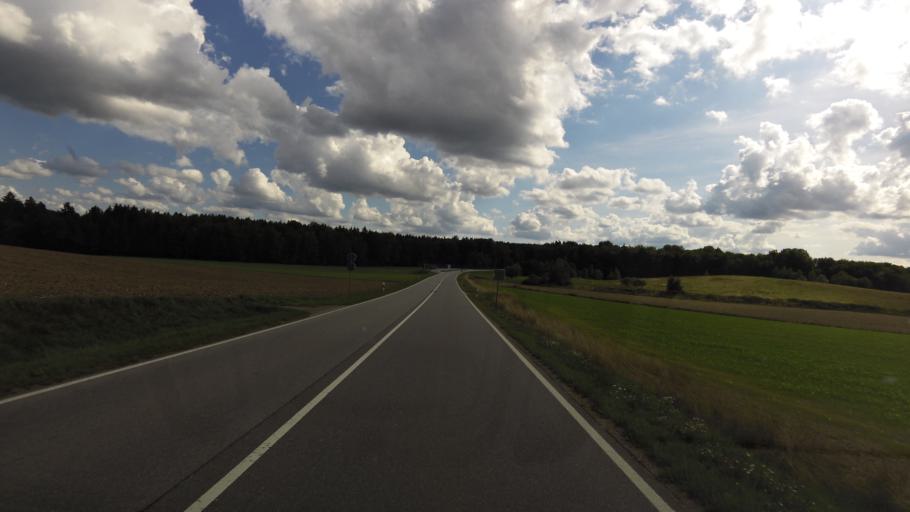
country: DE
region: Bavaria
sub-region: Upper Palatinate
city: Traitsching
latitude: 49.1863
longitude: 12.6529
